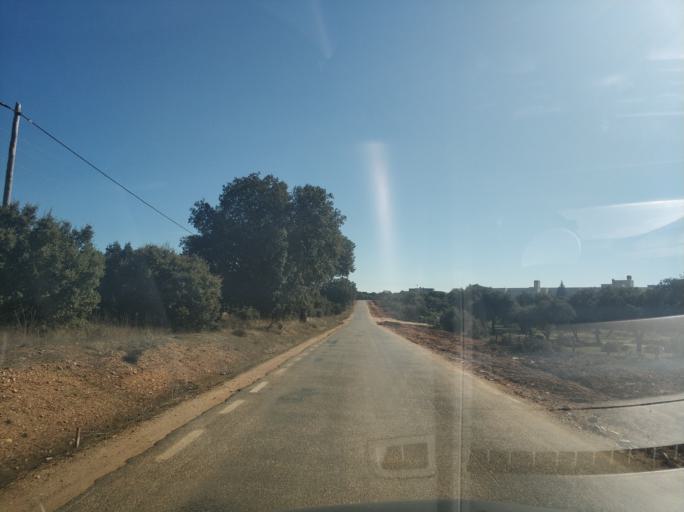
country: ES
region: Castille and Leon
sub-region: Provincia de Salamanca
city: Doninos de Salamanca
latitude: 40.9308
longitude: -5.7428
